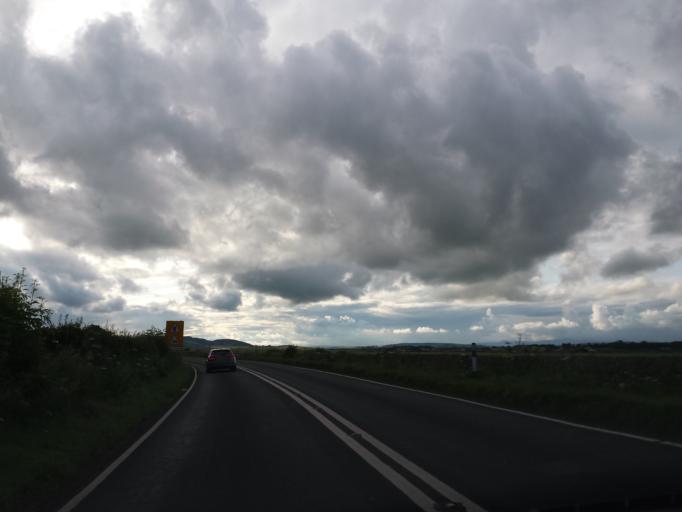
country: GB
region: Scotland
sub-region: Fife
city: Strathkinness
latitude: 56.3556
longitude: -2.8570
